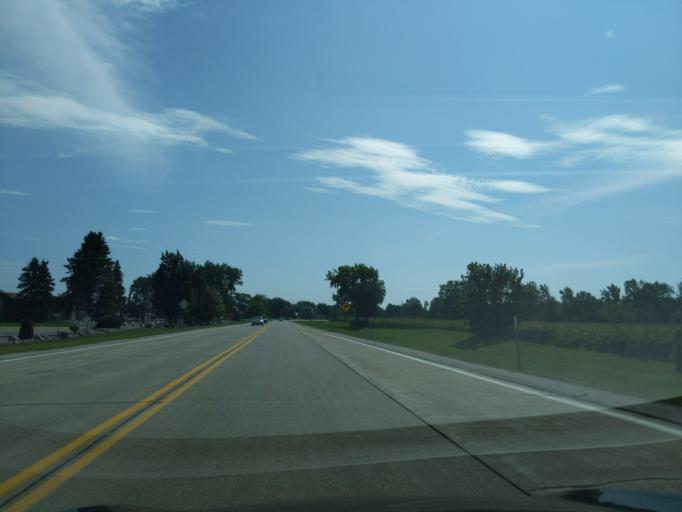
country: US
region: Michigan
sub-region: Saginaw County
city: Frankenmuth
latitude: 43.3138
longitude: -83.7388
